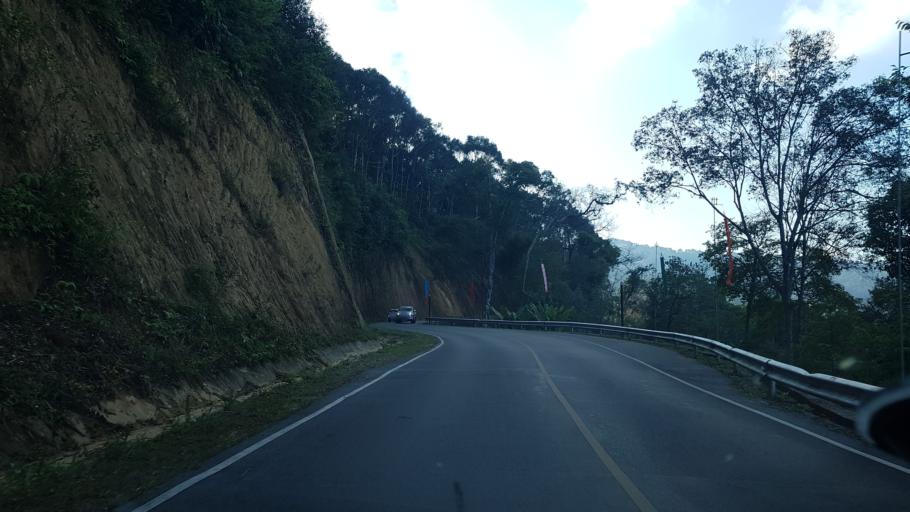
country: TH
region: Chiang Rai
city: Mae Fa Luang
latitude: 20.3274
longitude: 99.8299
